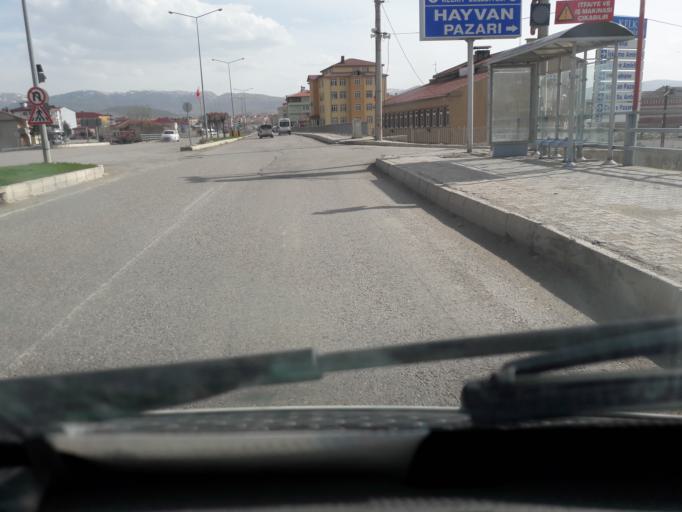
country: TR
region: Gumushane
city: Kelkit
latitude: 40.1379
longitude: 39.4334
